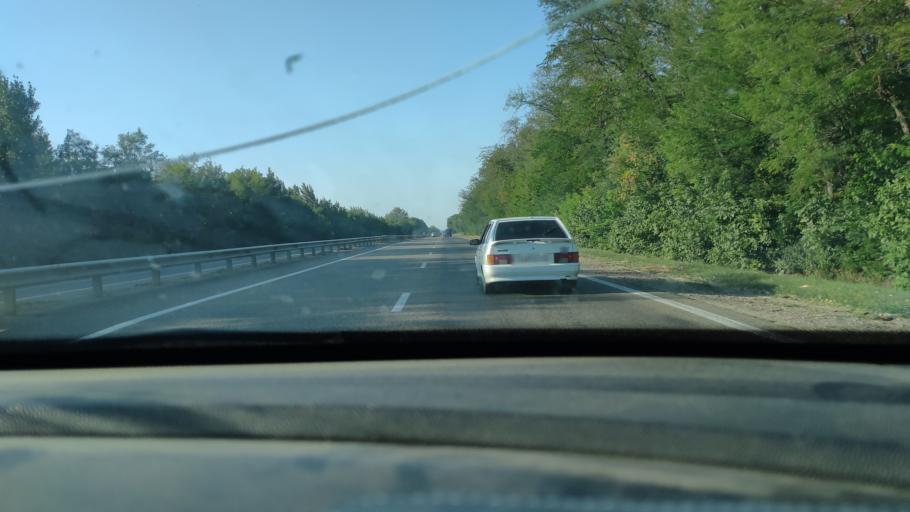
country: RU
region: Krasnodarskiy
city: Timashevsk
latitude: 45.5322
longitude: 38.9395
